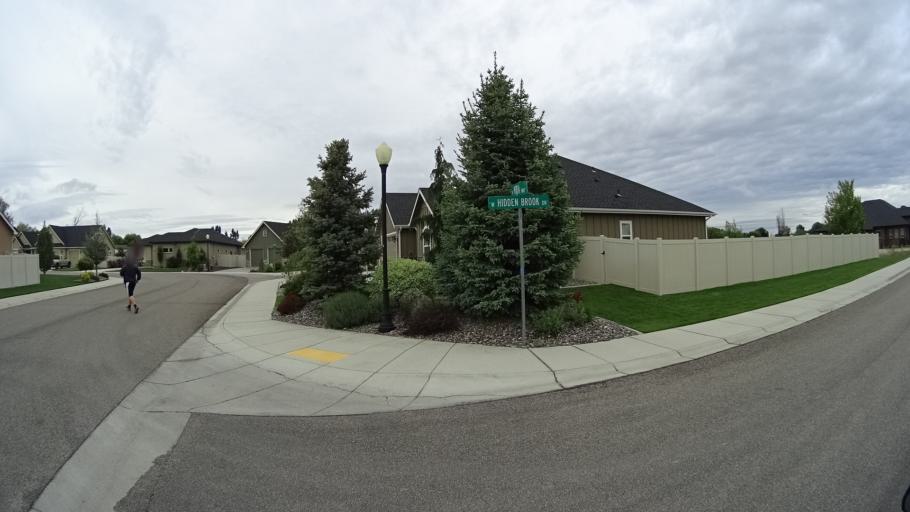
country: US
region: Idaho
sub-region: Ada County
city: Star
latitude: 43.7004
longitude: -116.4869
